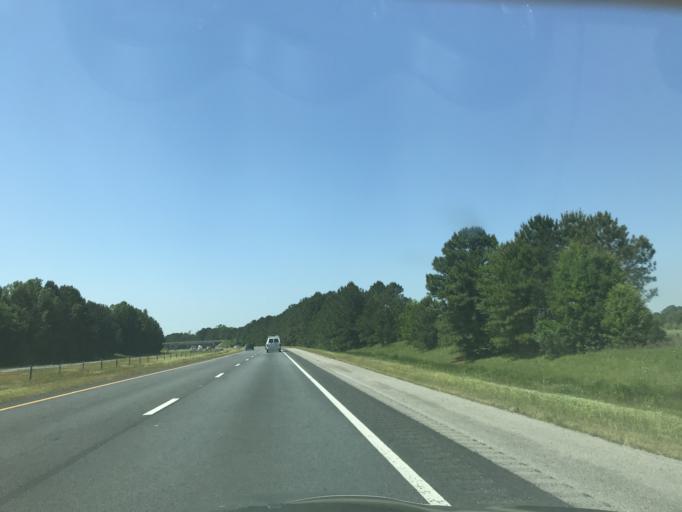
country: US
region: North Carolina
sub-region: Johnston County
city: Benson
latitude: 35.3372
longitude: -78.4618
